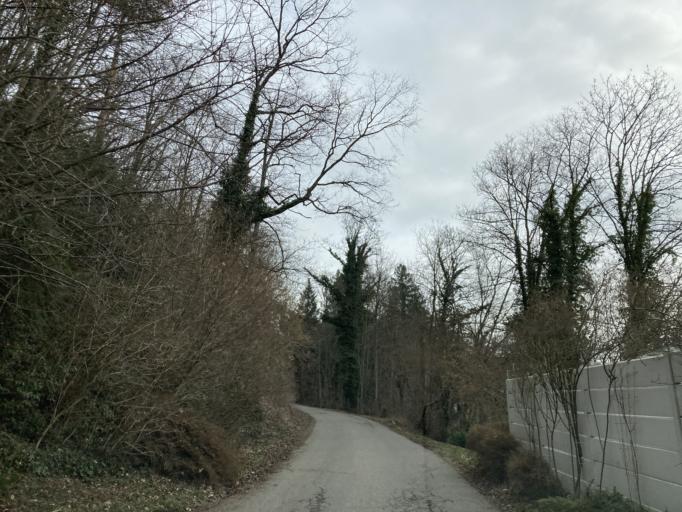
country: DE
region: Baden-Wuerttemberg
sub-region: Tuebingen Region
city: Rottenburg
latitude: 48.4552
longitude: 8.9031
